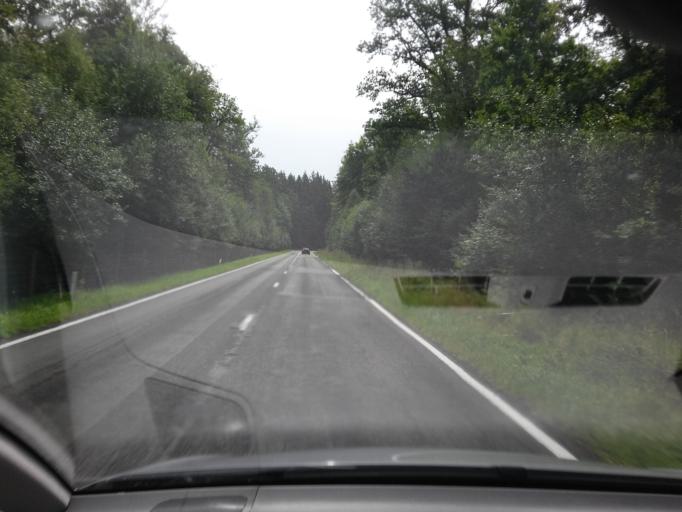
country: BE
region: Wallonia
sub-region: Province du Luxembourg
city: Chiny
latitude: 49.7717
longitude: 5.3582
